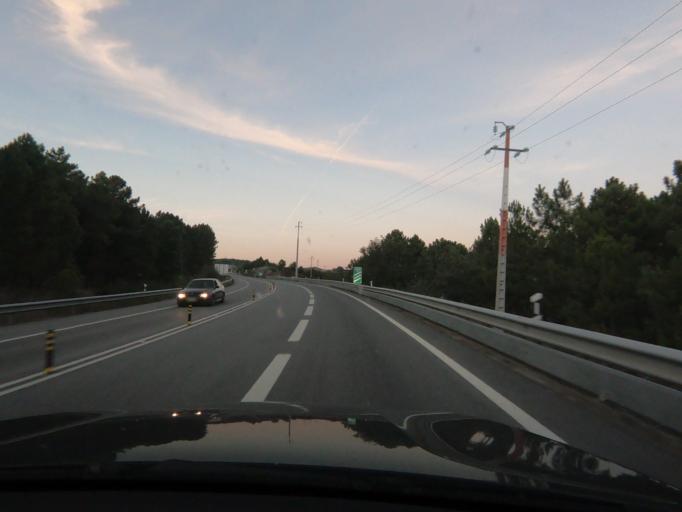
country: PT
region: Vila Real
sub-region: Vila Real
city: Vila Real
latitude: 41.3165
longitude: -7.7056
